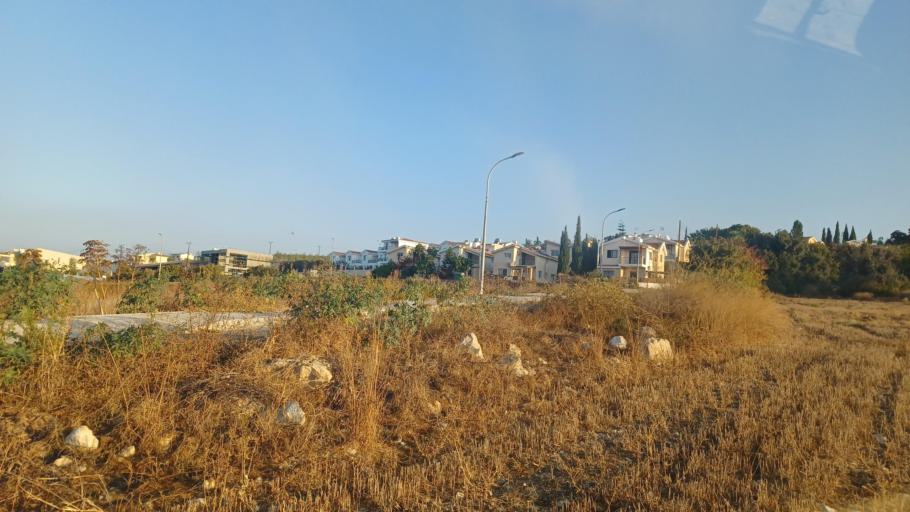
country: CY
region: Pafos
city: Mesogi
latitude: 34.8121
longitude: 32.4416
